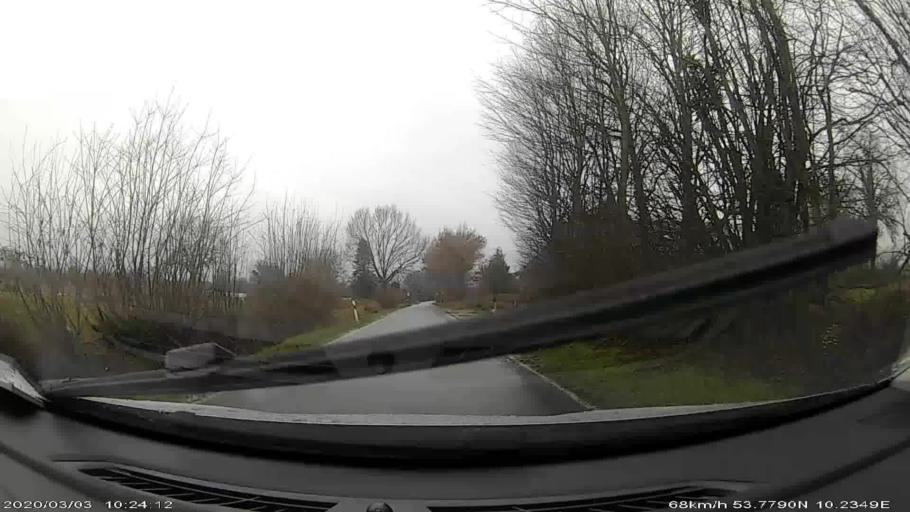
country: DE
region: Schleswig-Holstein
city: Sulfeld
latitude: 53.7777
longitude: 10.2298
